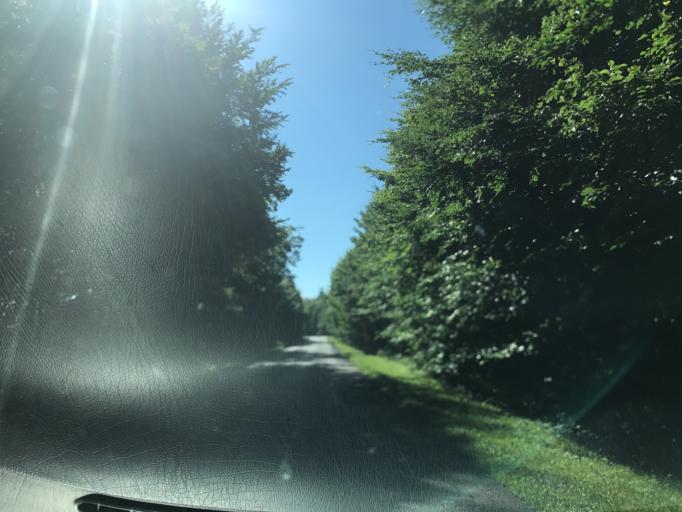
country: PL
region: Pomeranian Voivodeship
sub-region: Powiat bytowski
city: Czarna Dabrowka
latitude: 54.3779
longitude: 17.4929
